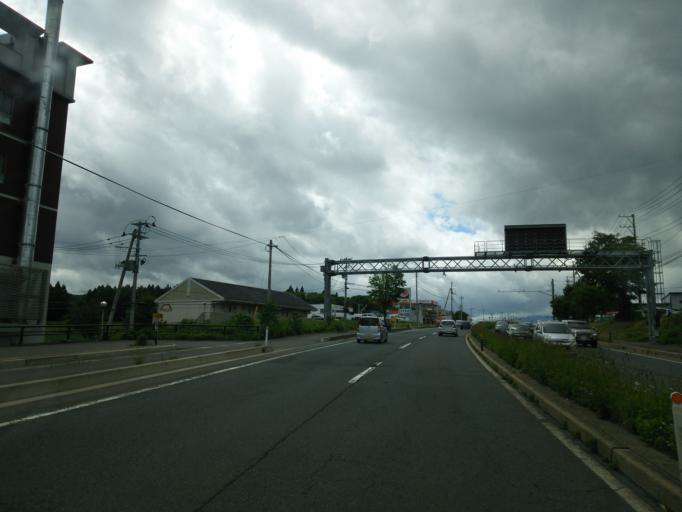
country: JP
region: Iwate
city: Shizukuishi
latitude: 39.6993
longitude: 141.0569
